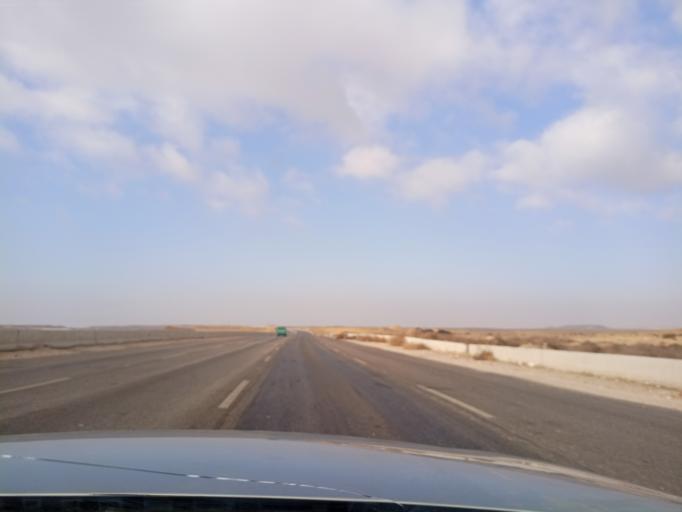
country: EG
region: Al Jizah
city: Al `Ayyat
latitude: 29.6716
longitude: 31.1959
